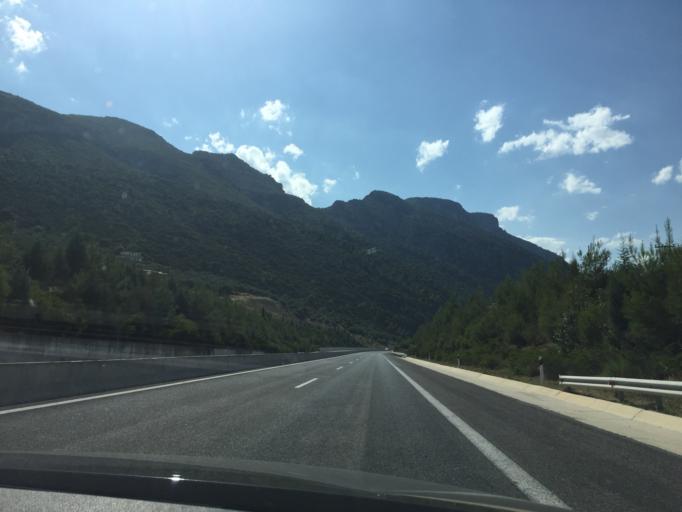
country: GR
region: Central Greece
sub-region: Nomos Fthiotidos
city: Ayios Konstandinos
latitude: 38.7482
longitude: 22.8584
